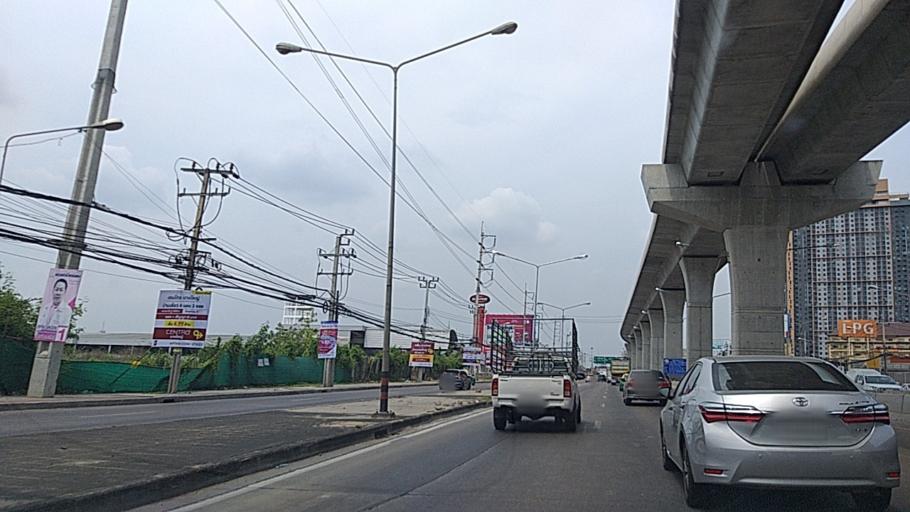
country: TH
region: Nonthaburi
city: Bang Bua Thong
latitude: 13.8744
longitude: 100.4180
